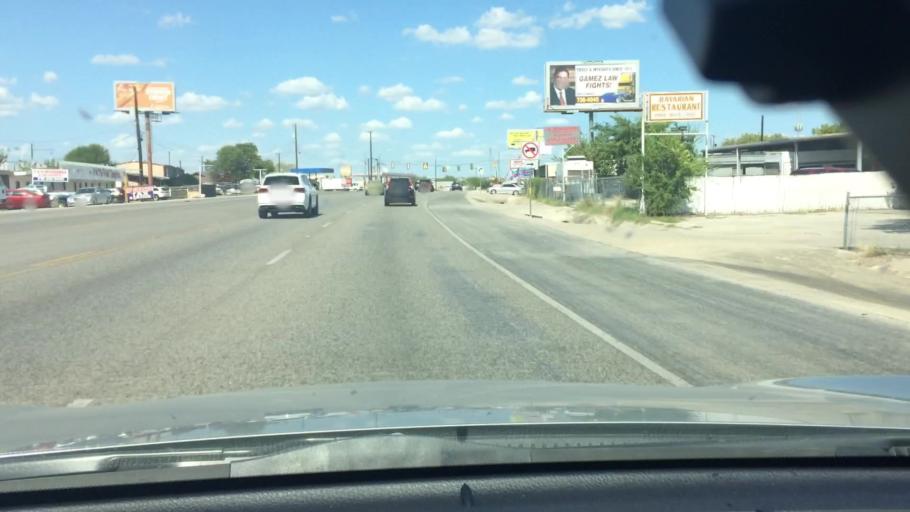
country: US
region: Texas
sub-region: Bexar County
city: Kirby
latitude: 29.4734
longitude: -98.3823
